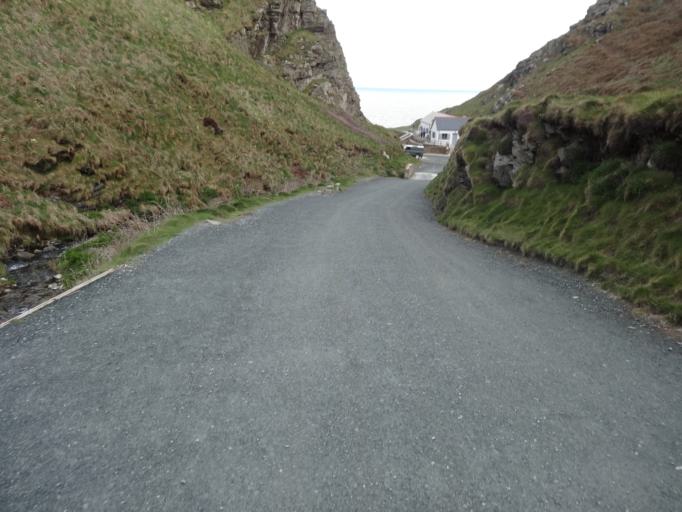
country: GB
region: England
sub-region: Cornwall
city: Tintagel
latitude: 50.6670
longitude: -4.7573
